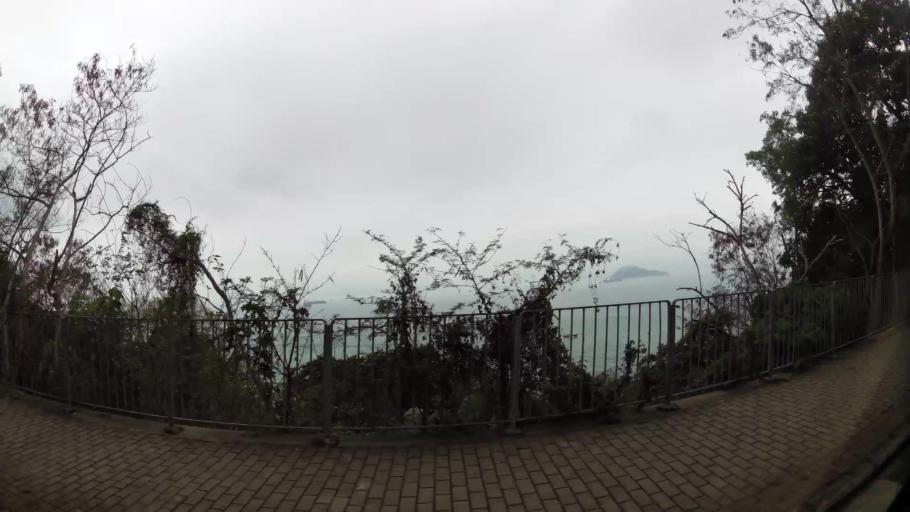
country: HK
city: Hong Kong
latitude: 22.2762
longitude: 114.1174
